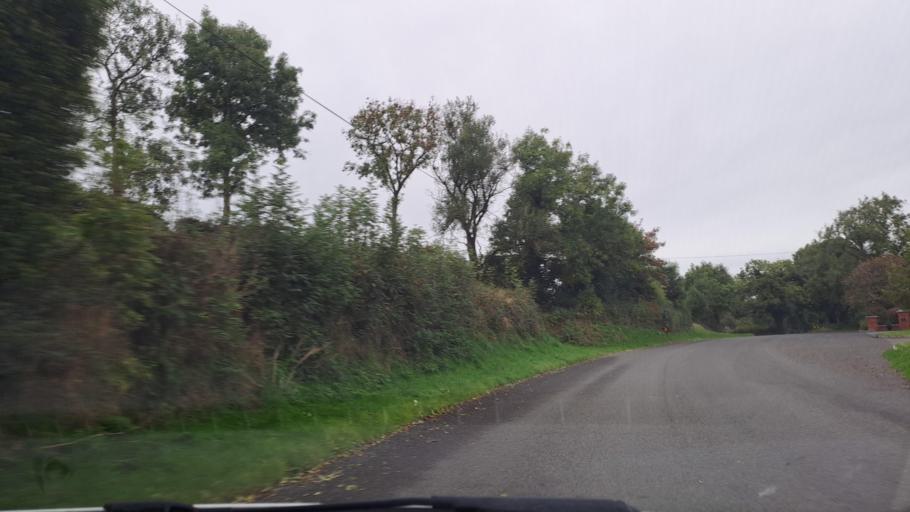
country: IE
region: Ulster
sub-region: County Monaghan
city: Carrickmacross
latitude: 53.9497
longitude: -6.6872
